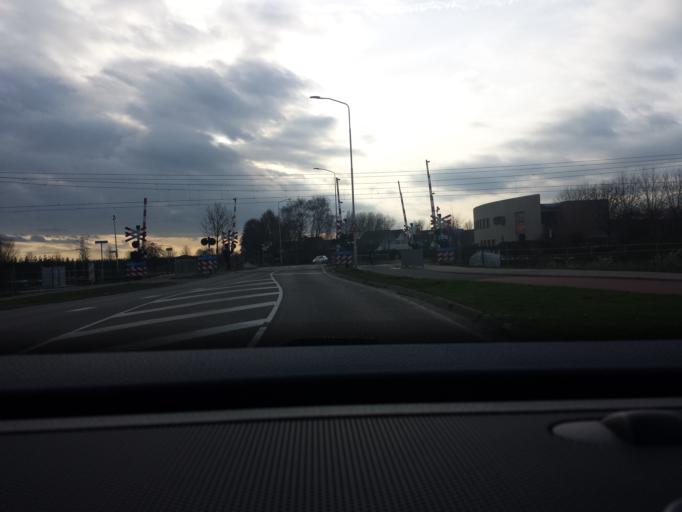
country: NL
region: Gelderland
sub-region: Gemeente Duiven
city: Duiven
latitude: 51.9412
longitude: 6.0214
